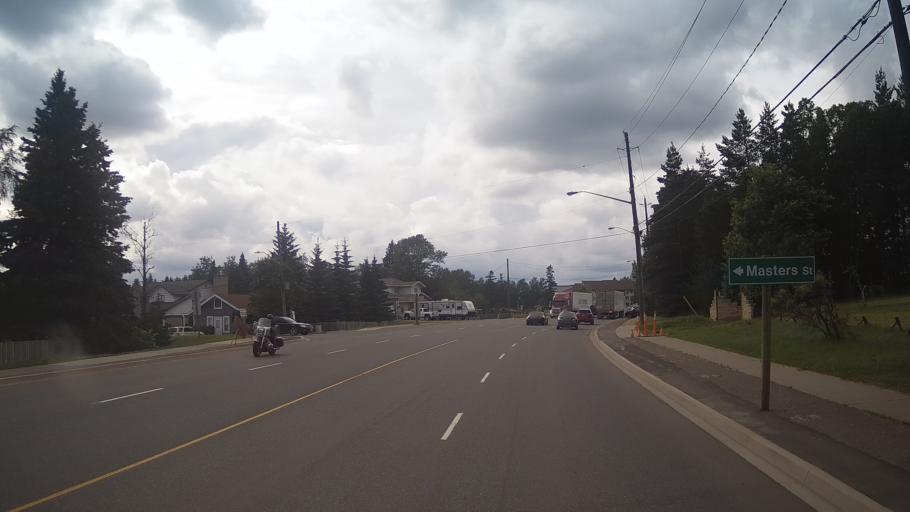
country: CA
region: Ontario
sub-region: Thunder Bay District
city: Thunder Bay
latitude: 48.4546
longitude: -89.2616
